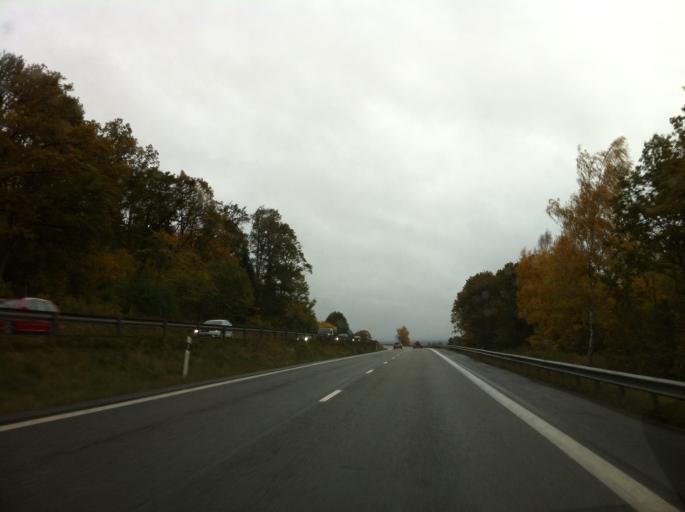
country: SE
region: Joenkoeping
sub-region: Jonkopings Kommun
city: Kaxholmen
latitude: 57.8838
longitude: 14.2815
